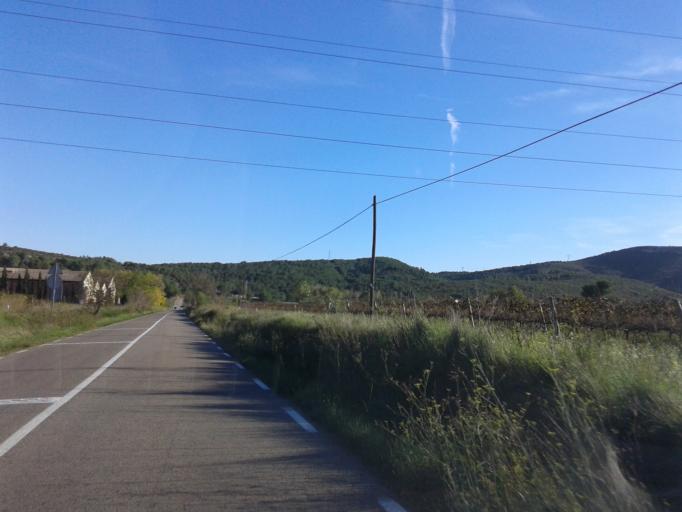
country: ES
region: Catalonia
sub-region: Provincia de Barcelona
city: Avinyonet del Penedes
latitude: 41.3407
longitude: 1.7451
